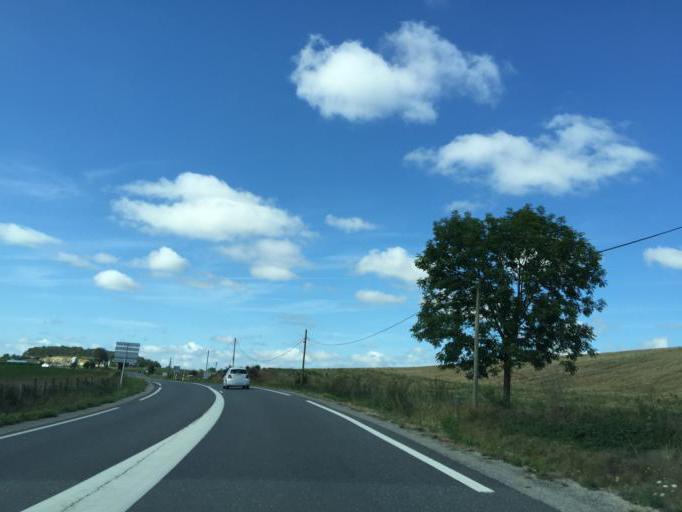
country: FR
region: Midi-Pyrenees
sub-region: Departement de l'Aveyron
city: Rieupeyroux
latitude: 44.3312
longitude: 2.1961
